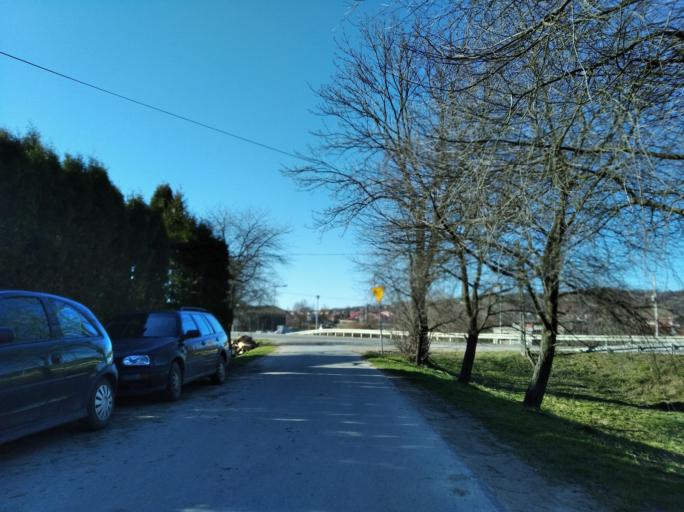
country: PL
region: Subcarpathian Voivodeship
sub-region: Powiat strzyzowski
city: Strzyzow
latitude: 49.8636
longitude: 21.7980
